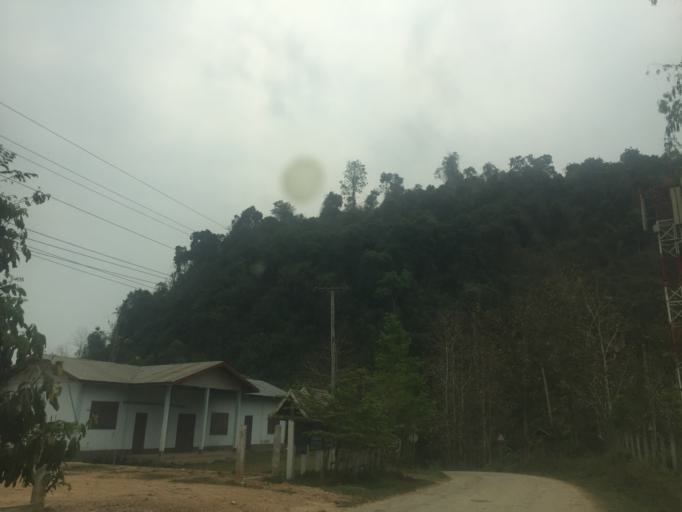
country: LA
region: Vientiane
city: Muang Sanakham
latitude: 18.3882
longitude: 101.5235
